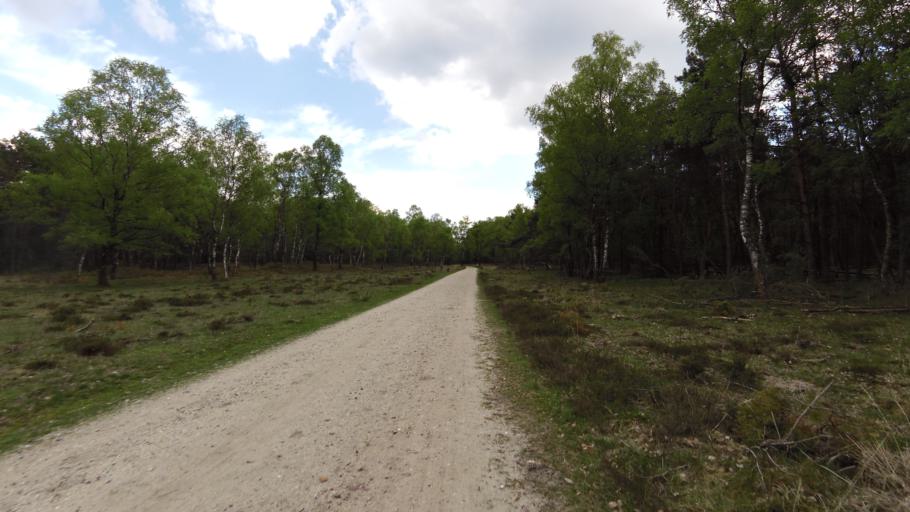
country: NL
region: Gelderland
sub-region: Gemeente Rheden
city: Rheden
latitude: 52.0399
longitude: 6.0076
